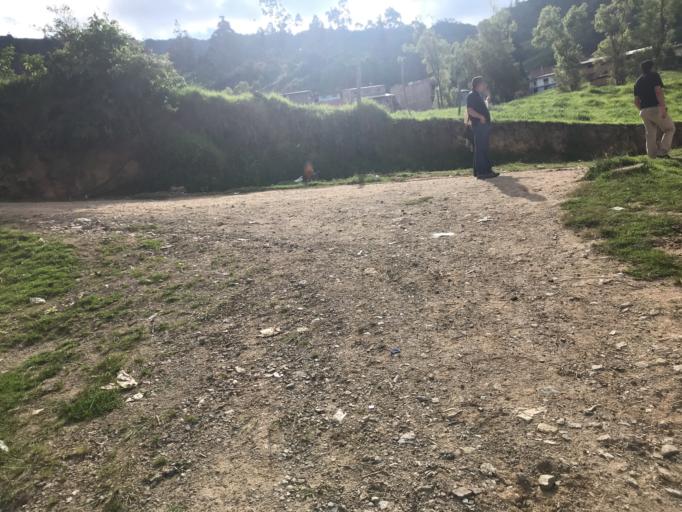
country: PE
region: Cajamarca
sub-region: Provincia de Chota
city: Querocoto
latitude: -6.3574
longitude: -79.0344
